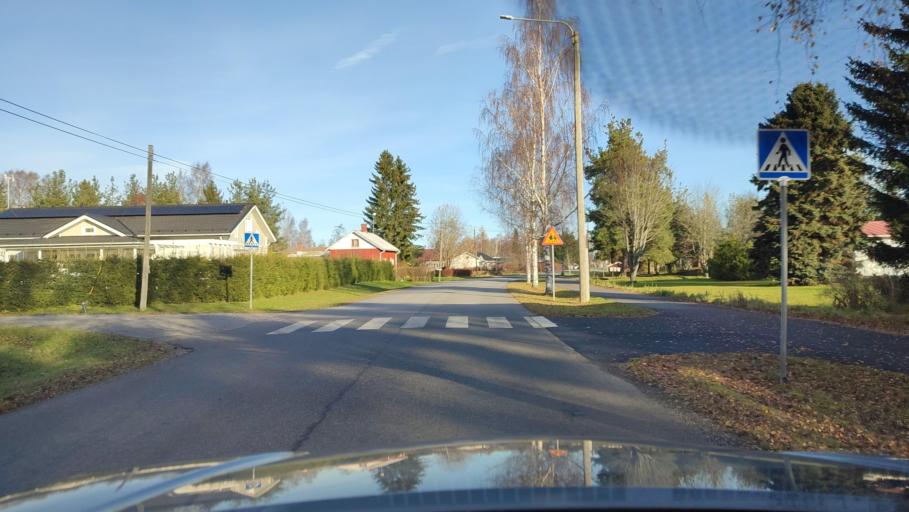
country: FI
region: Southern Ostrobothnia
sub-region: Suupohja
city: Teuva
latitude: 62.4768
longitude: 21.7463
